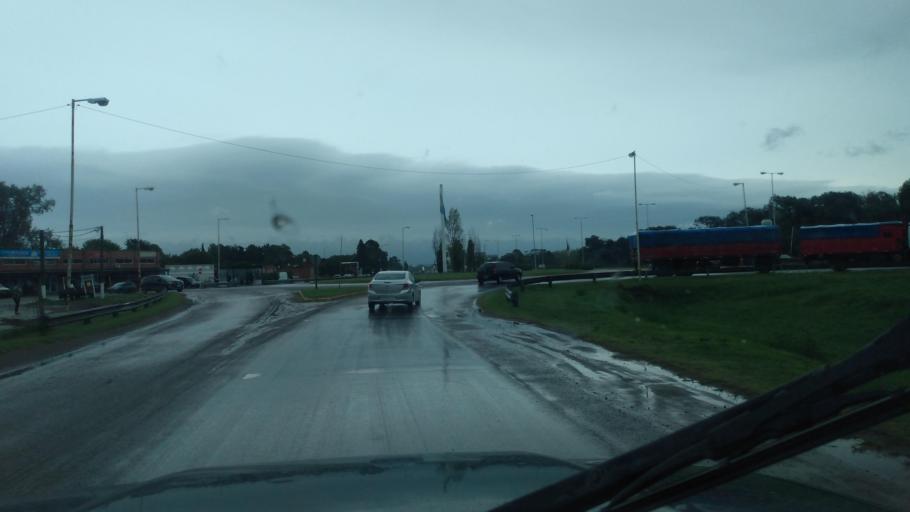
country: AR
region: Buenos Aires
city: Capilla del Senor
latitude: -34.3918
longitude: -59.0381
